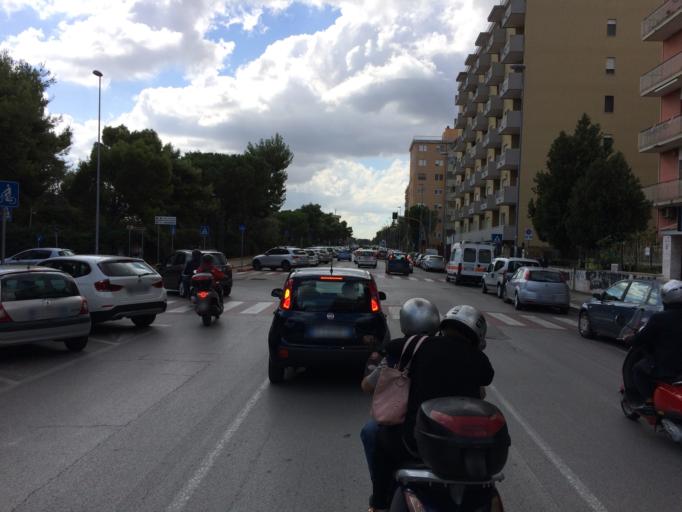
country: IT
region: Apulia
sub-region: Provincia di Bari
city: Bari
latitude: 41.1041
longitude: 16.8736
